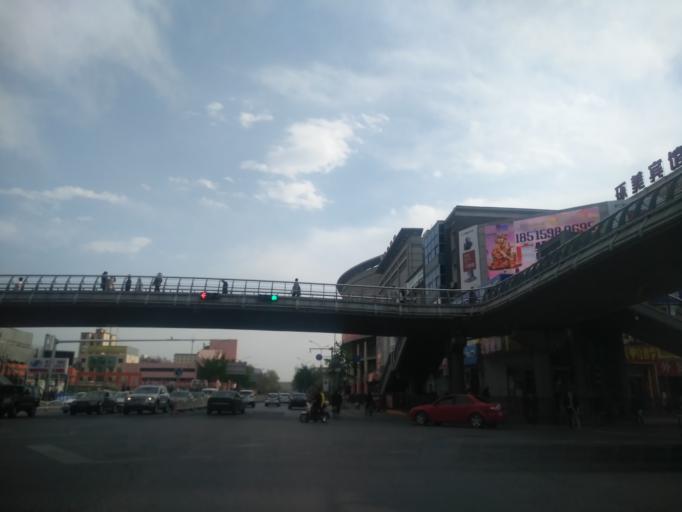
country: CN
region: Beijing
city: Xingfeng
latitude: 39.7306
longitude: 116.3333
